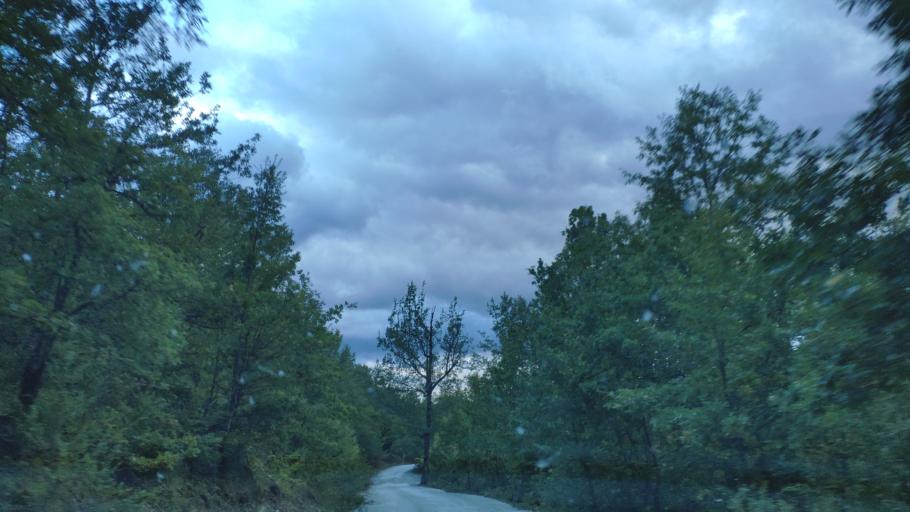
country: AL
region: Korce
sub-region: Rrethi i Kolonjes
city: Erseke
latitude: 40.2613
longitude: 20.8585
